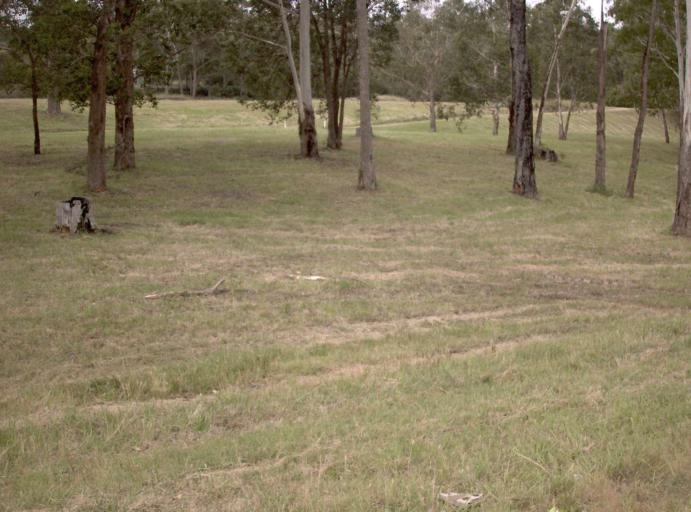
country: AU
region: Victoria
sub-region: East Gippsland
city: Lakes Entrance
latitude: -37.7304
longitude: 148.0963
